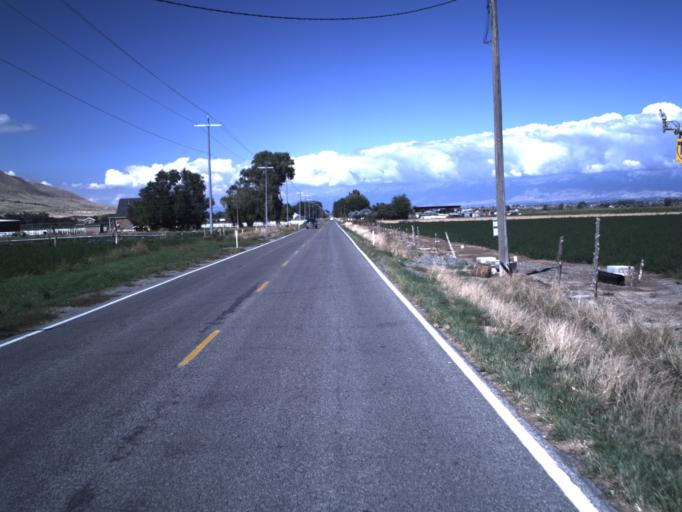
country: US
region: Utah
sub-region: Utah County
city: West Mountain
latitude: 40.0461
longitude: -111.7873
